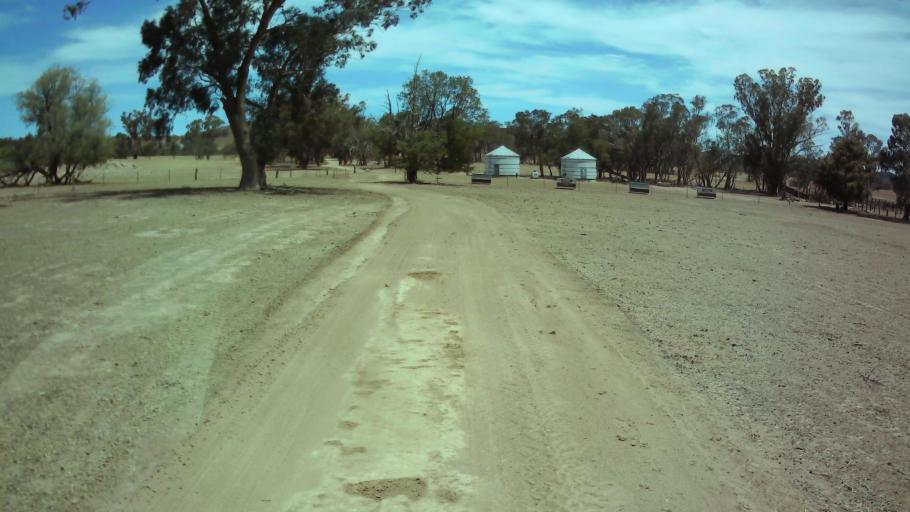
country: AU
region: New South Wales
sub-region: Weddin
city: Grenfell
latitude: -33.7769
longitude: 148.1516
